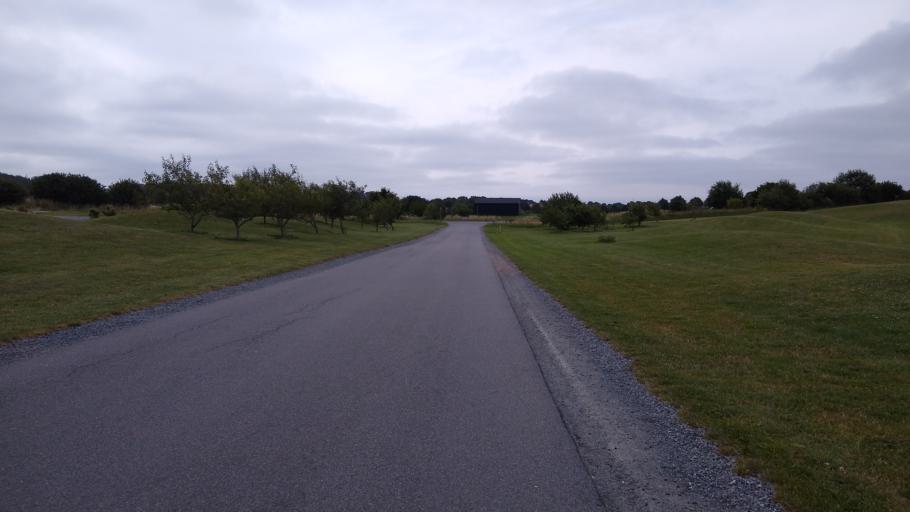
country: DK
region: South Denmark
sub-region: Vejle Kommune
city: Brejning
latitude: 55.6568
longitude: 9.6845
